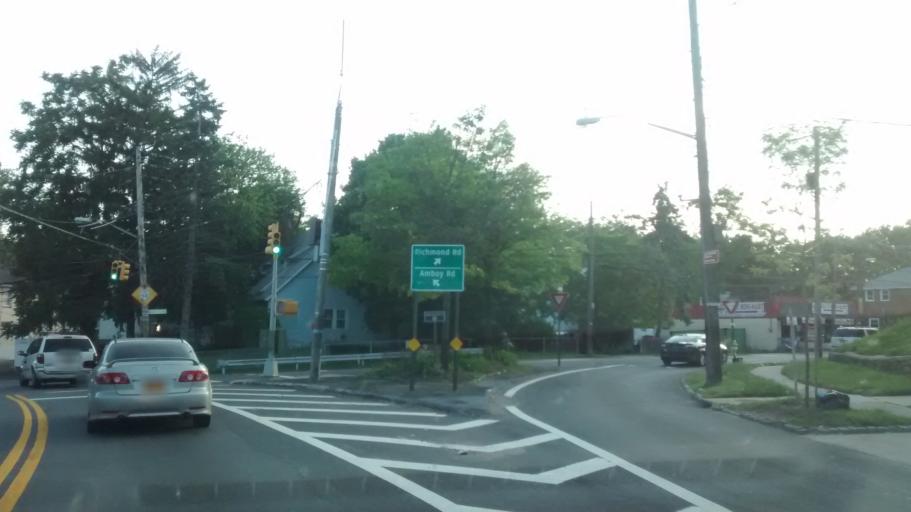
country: US
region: New York
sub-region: Richmond County
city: Staten Island
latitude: 40.5752
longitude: -74.1214
